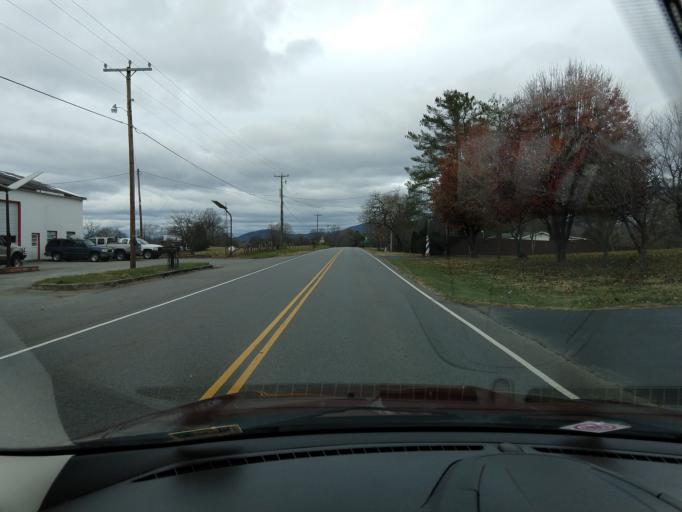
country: US
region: Virginia
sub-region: Botetourt County
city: Blue Ridge
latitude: 37.2605
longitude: -79.7304
